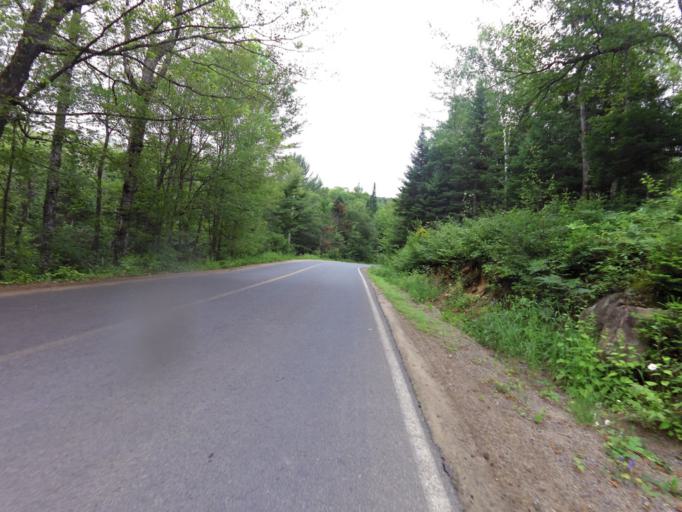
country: CA
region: Quebec
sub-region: Laurentides
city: Brownsburg-Chatham
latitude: 45.9096
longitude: -74.5965
